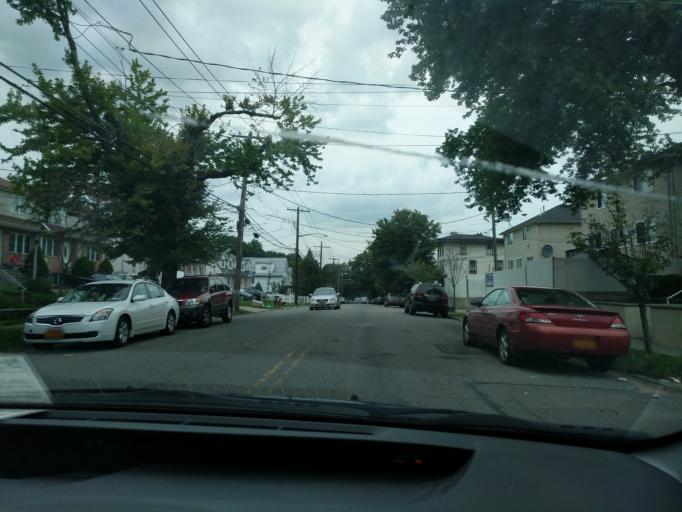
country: US
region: New York
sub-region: Richmond County
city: Bloomfield
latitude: 40.6370
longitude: -74.1661
